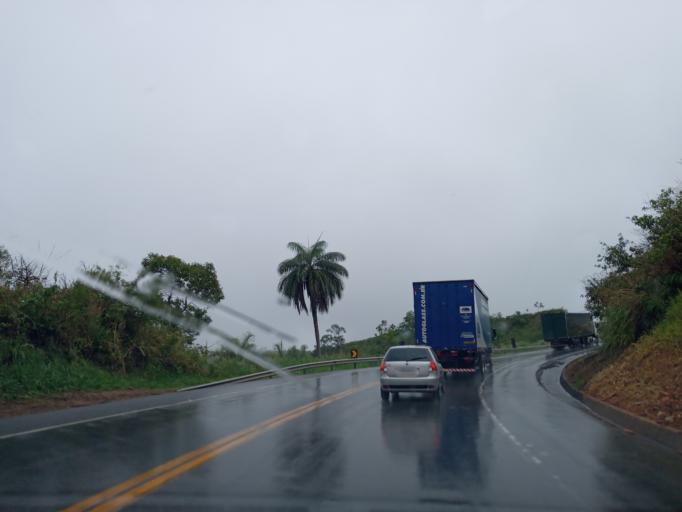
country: BR
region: Minas Gerais
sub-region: Luz
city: Luz
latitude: -19.7188
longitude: -45.8816
